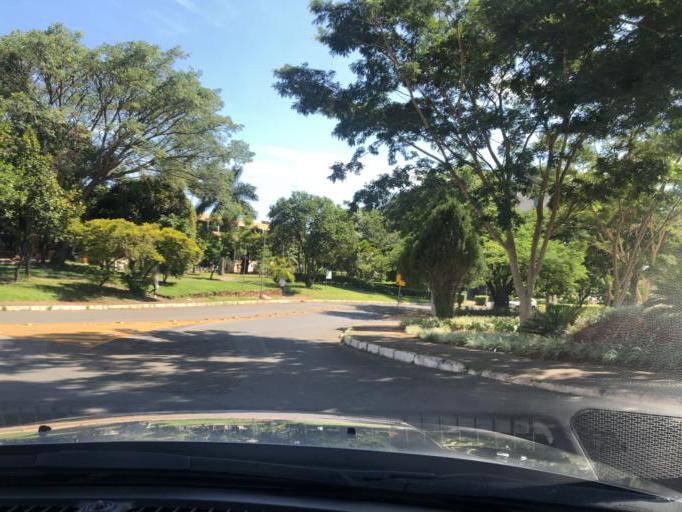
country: BR
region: Federal District
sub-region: Brasilia
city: Brasilia
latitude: -15.7996
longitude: -47.9211
